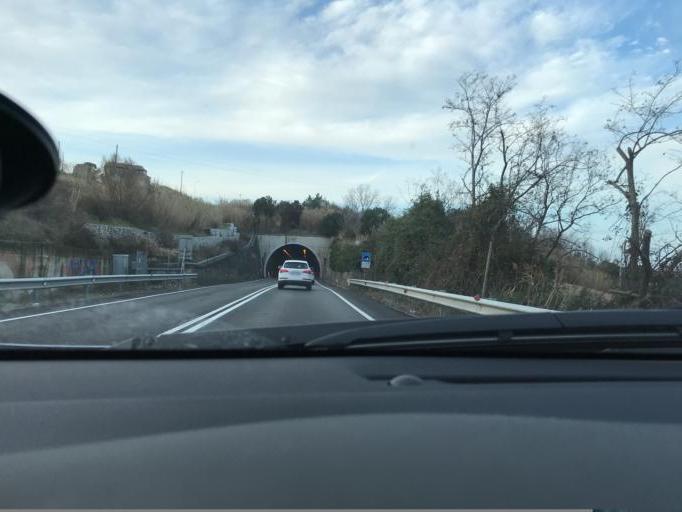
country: IT
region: The Marches
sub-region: Provincia di Ancona
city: Falconara Marittima
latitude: 43.6102
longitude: 13.4128
